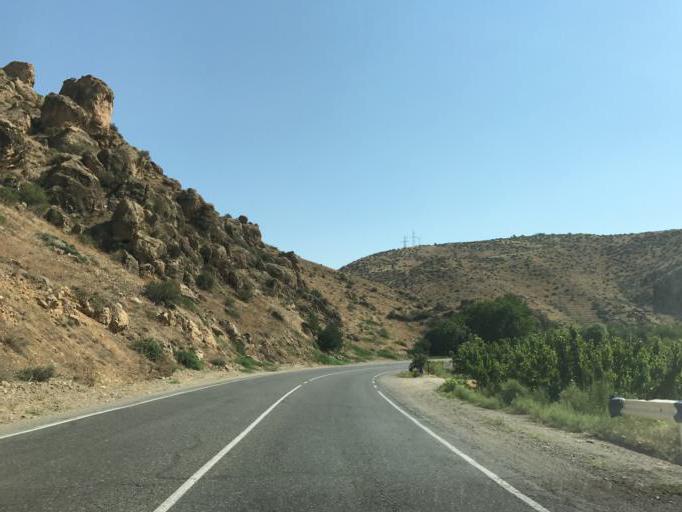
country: AM
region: Vayots' Dzori Marz
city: Areni
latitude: 39.7325
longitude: 45.1960
